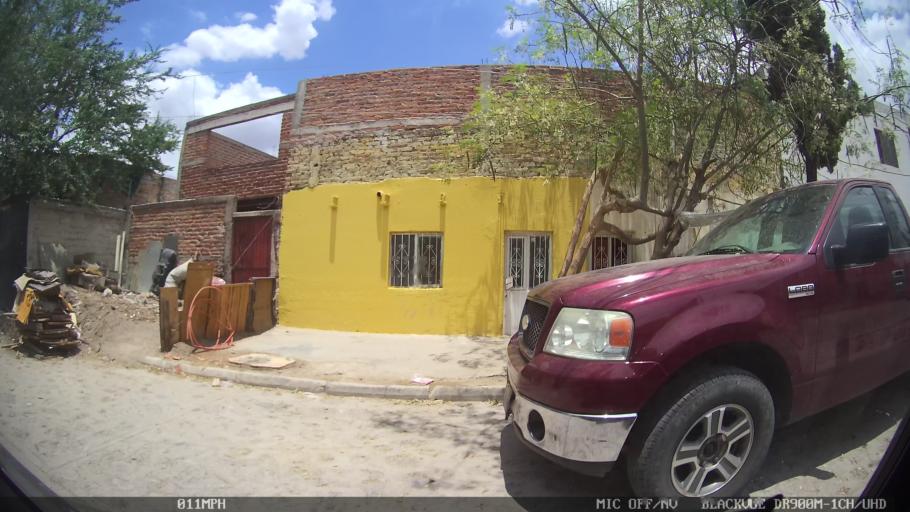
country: MX
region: Jalisco
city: Tlaquepaque
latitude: 20.6377
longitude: -103.2648
